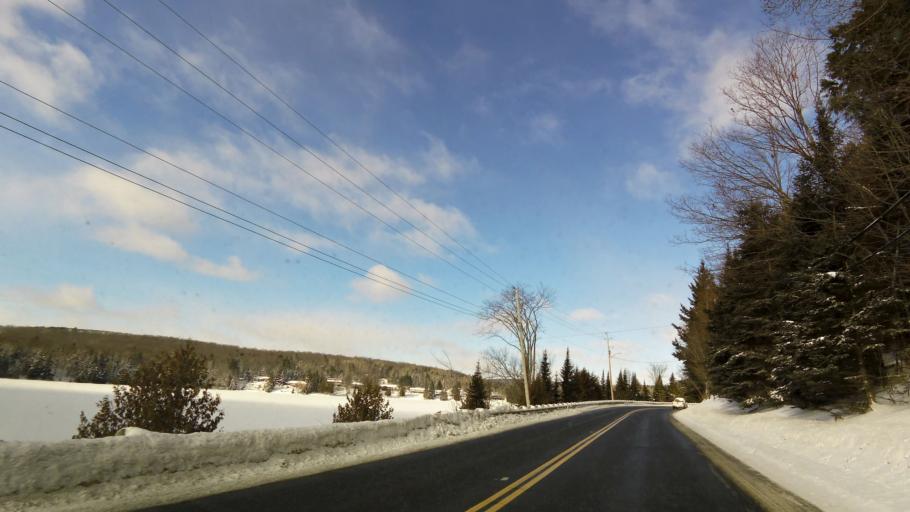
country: CA
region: Ontario
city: Bancroft
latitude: 45.0518
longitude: -78.5147
